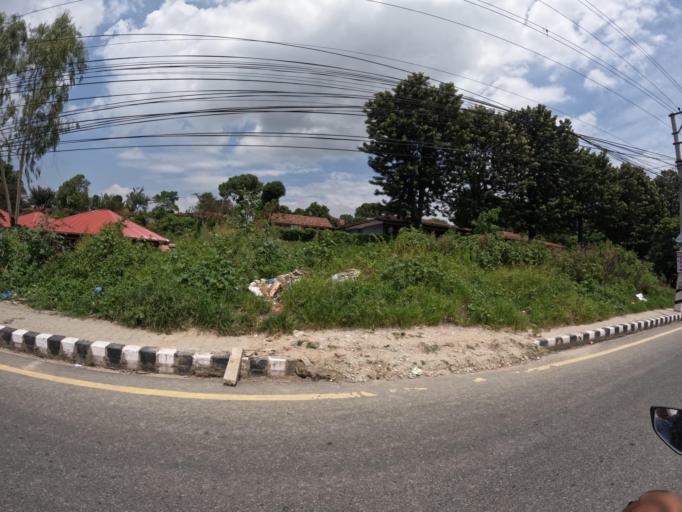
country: NP
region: Central Region
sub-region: Bagmati Zone
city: Kathmandu
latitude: 27.6828
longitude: 85.3712
